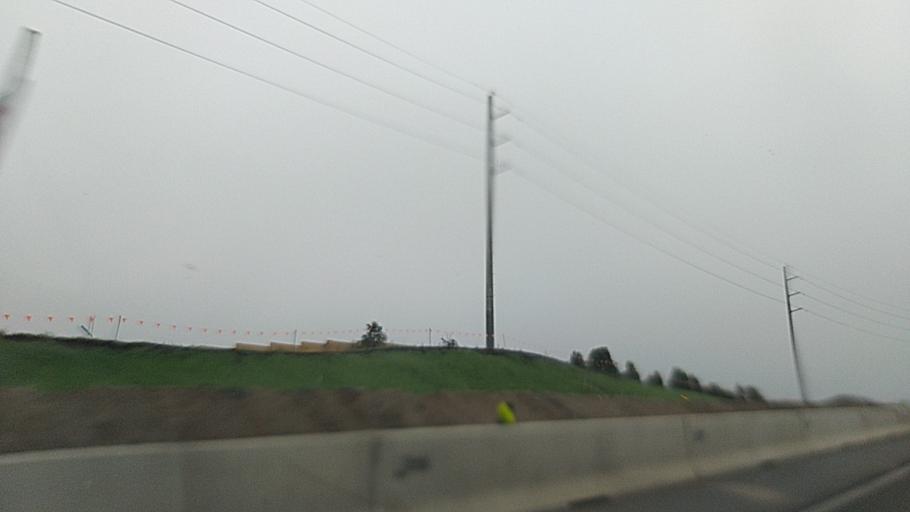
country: AU
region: New South Wales
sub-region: Camden
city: Narellan
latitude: -34.0020
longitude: 150.7227
